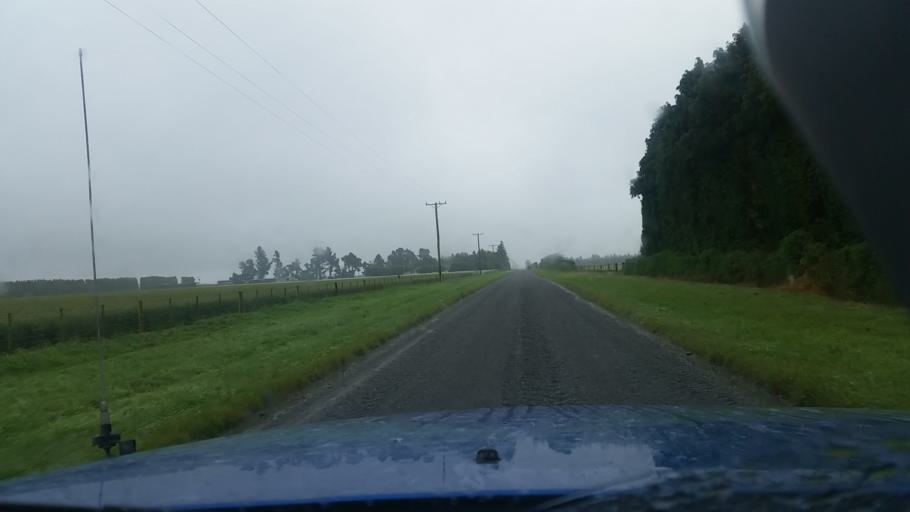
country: NZ
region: Canterbury
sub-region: Ashburton District
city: Rakaia
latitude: -43.6932
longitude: 171.8548
